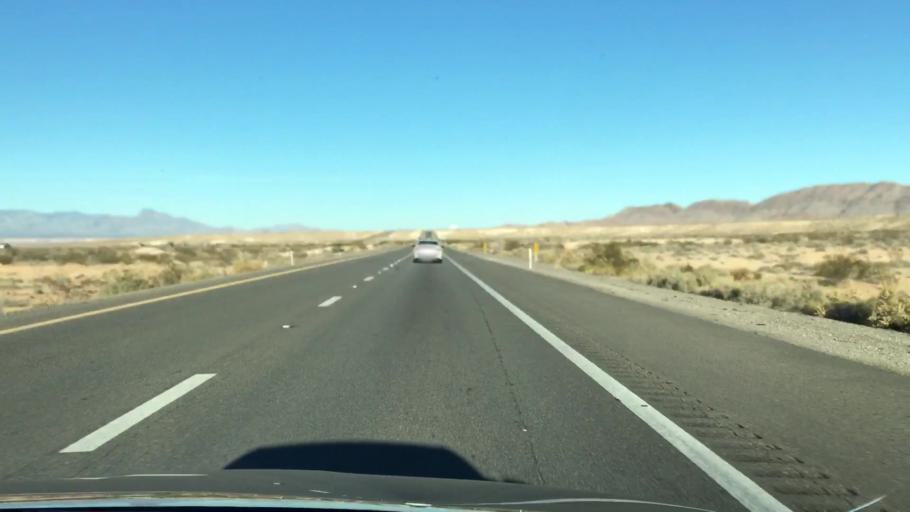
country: US
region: Nevada
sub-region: Clark County
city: Moapa Town
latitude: 36.5587
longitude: -114.6868
